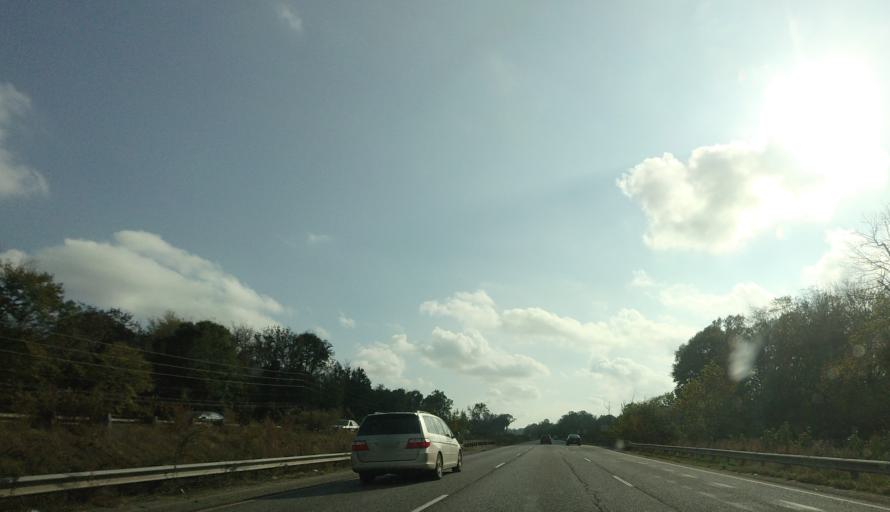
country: US
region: Georgia
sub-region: Bibb County
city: Macon
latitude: 32.7684
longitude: -83.6602
